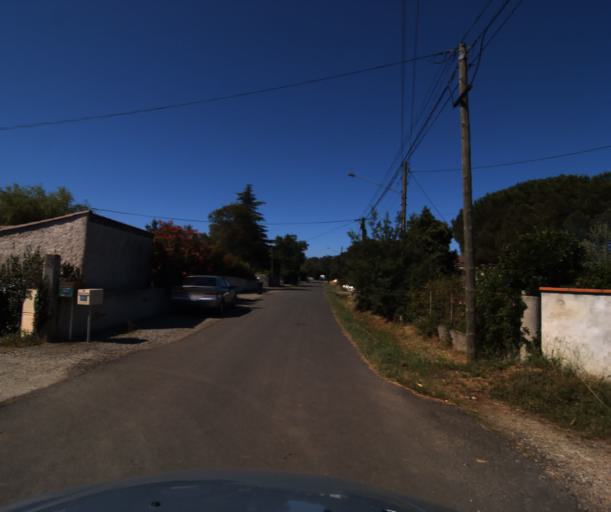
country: FR
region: Midi-Pyrenees
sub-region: Departement de la Haute-Garonne
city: Eaunes
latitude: 43.4229
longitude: 1.3394
